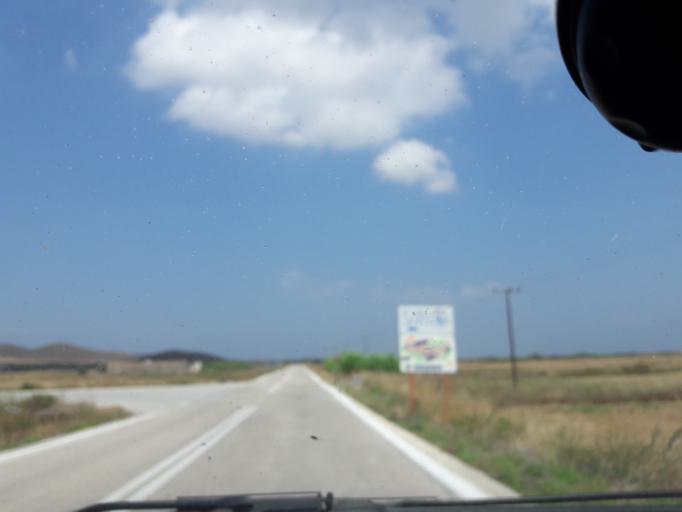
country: GR
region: North Aegean
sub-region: Nomos Lesvou
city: Myrina
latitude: 39.9617
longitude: 25.3700
